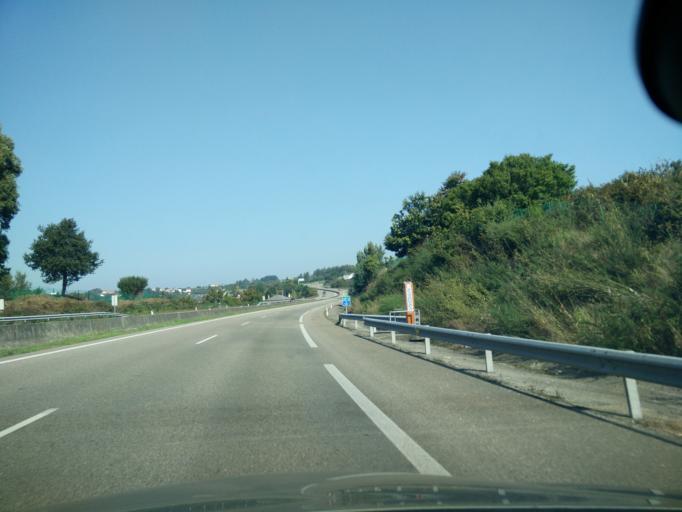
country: ES
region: Galicia
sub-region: Provincia da Coruna
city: Mino
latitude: 43.3552
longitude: -8.2026
